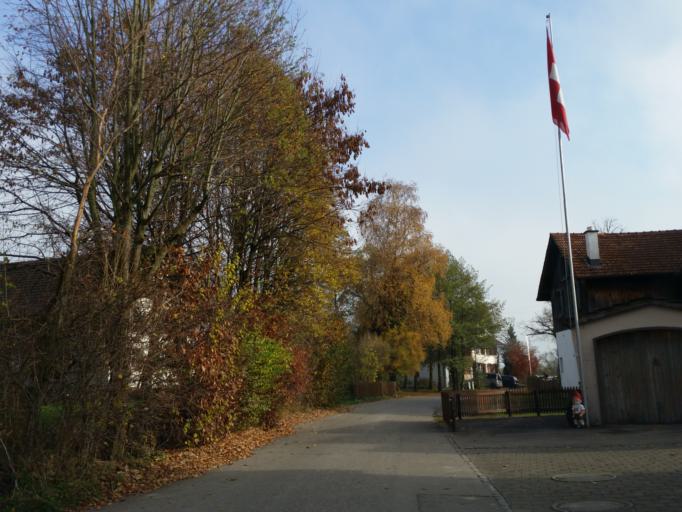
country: CH
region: Thurgau
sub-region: Arbon District
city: Egnach
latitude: 47.5309
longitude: 9.4072
